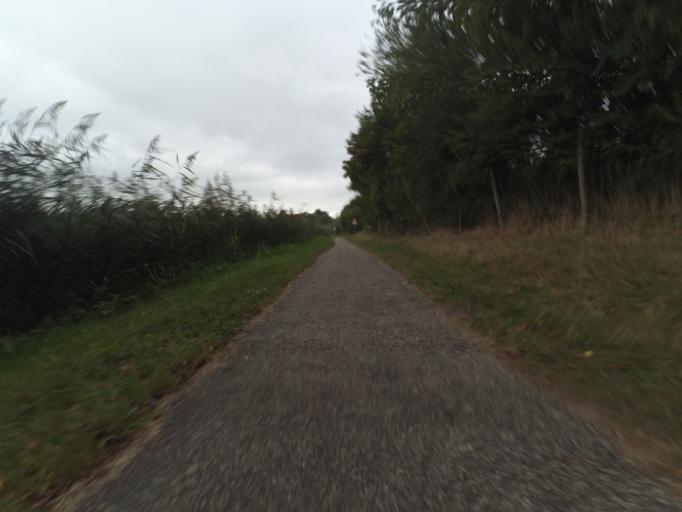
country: NL
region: Utrecht
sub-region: Gemeente Rhenen
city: Rhenen
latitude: 51.9581
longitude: 5.6096
